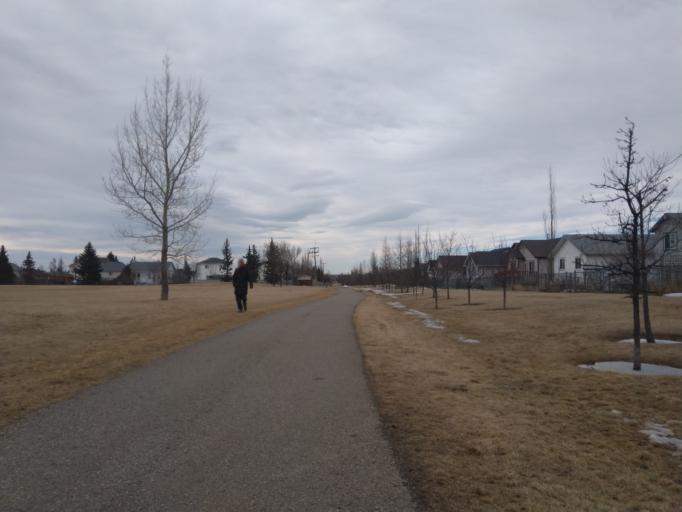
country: CA
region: Alberta
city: Calgary
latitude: 51.1641
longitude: -114.0480
